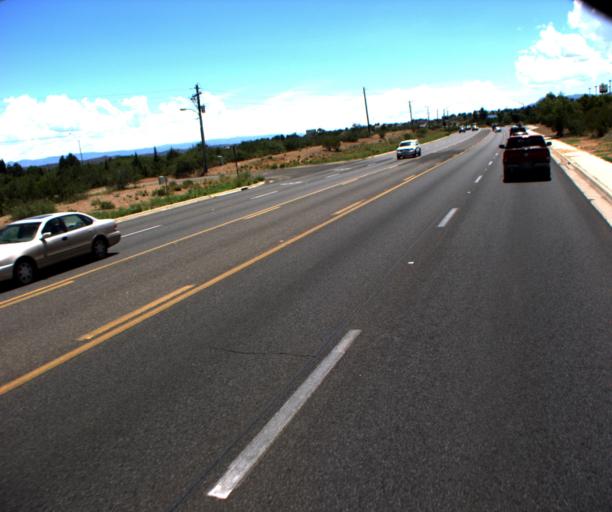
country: US
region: Arizona
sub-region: Yavapai County
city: Verde Village
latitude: 34.7169
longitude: -112.0008
